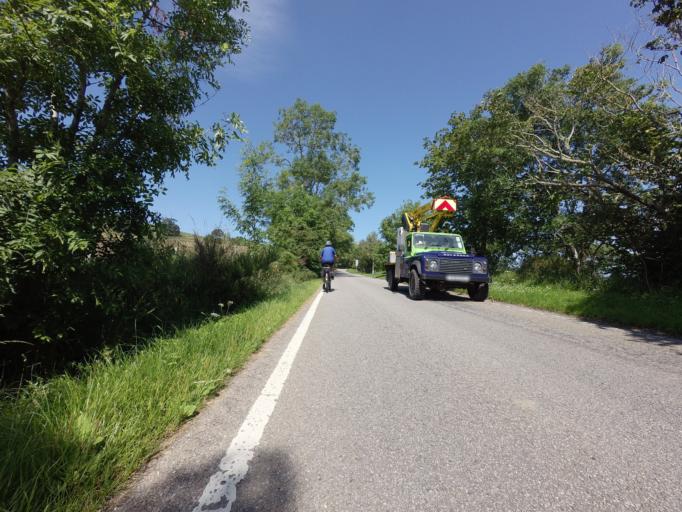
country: GB
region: Scotland
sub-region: Highland
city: Dingwall
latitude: 57.6117
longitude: -4.4158
